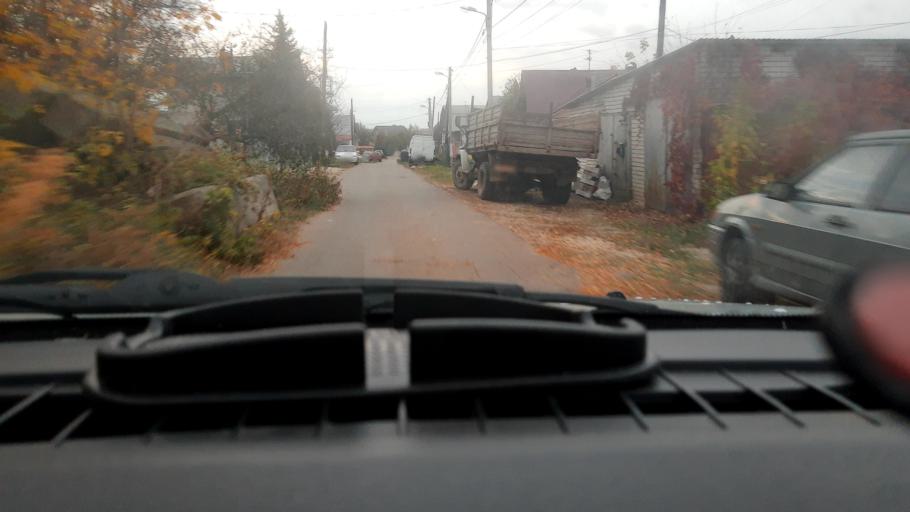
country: RU
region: Nizjnij Novgorod
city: Nizhniy Novgorod
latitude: 56.2543
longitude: 43.9930
